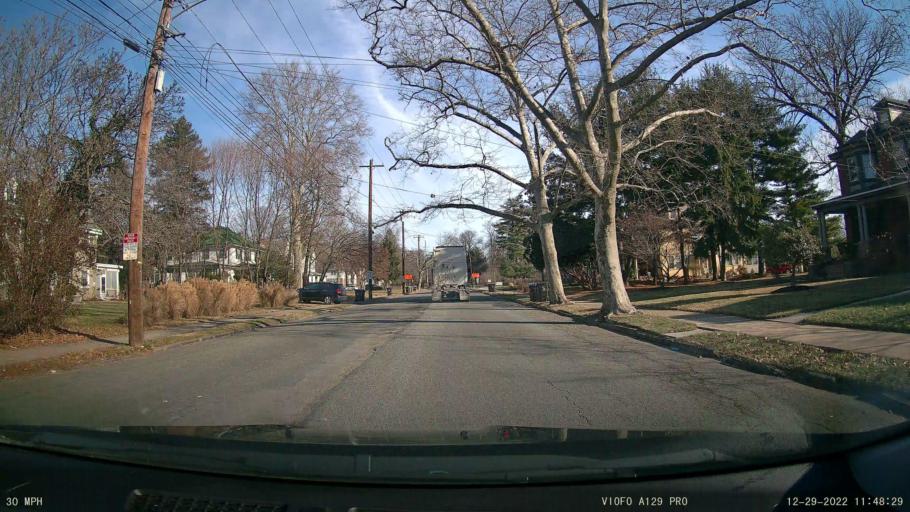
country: US
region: Pennsylvania
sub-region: Montgomery County
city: Norristown
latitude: 40.1257
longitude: -75.3300
